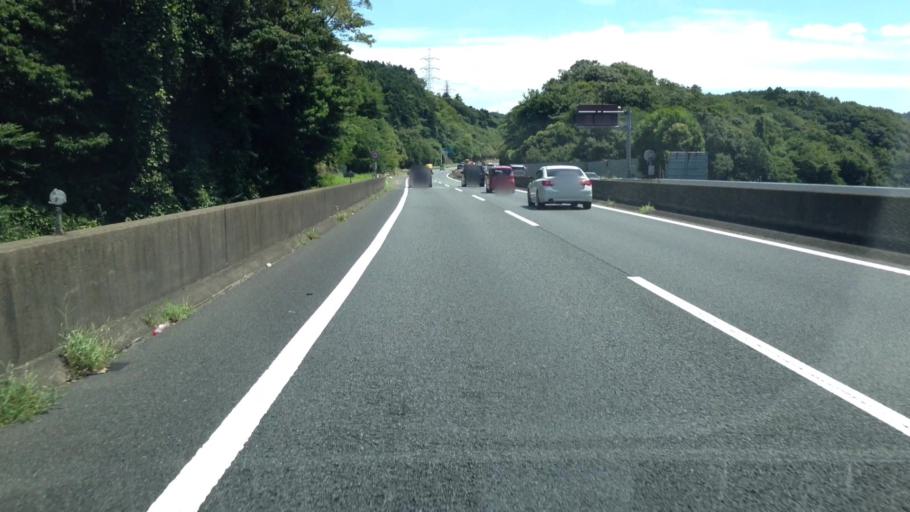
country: JP
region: Kanagawa
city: Zushi
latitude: 35.3034
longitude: 139.6120
